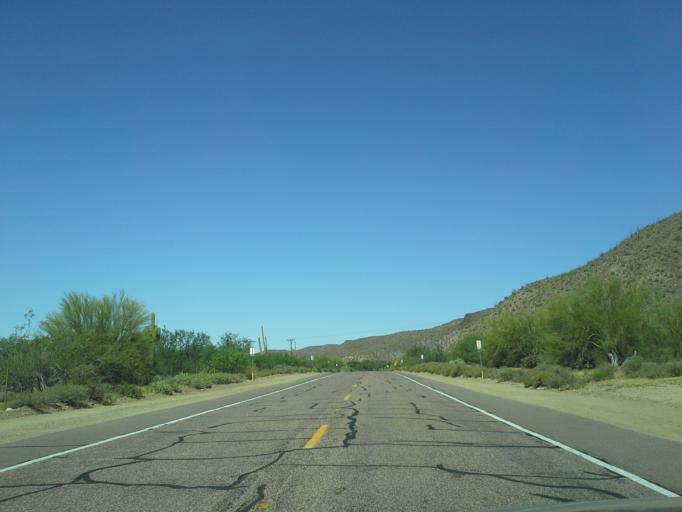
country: US
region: Arizona
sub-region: Pinal County
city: Apache Junction
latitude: 33.5528
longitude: -111.5646
